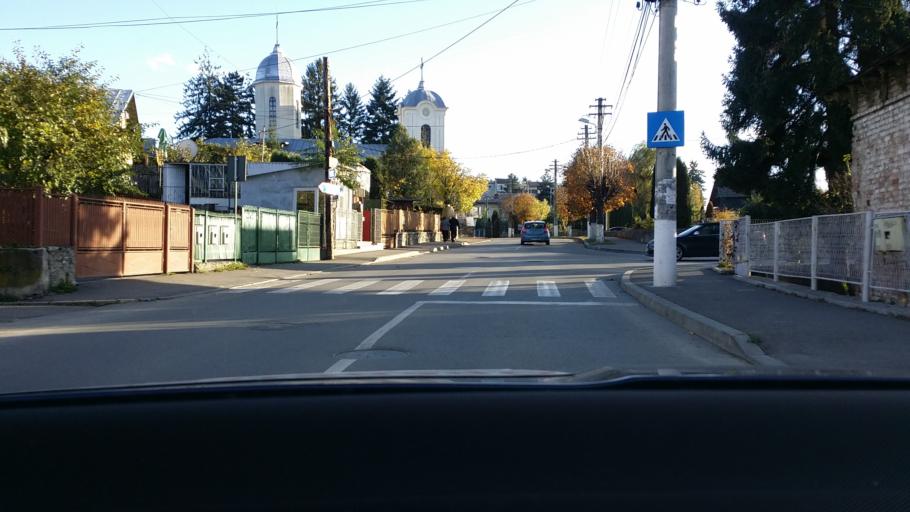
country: RO
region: Prahova
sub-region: Municipiul Campina
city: Campina
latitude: 45.1332
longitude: 25.7344
